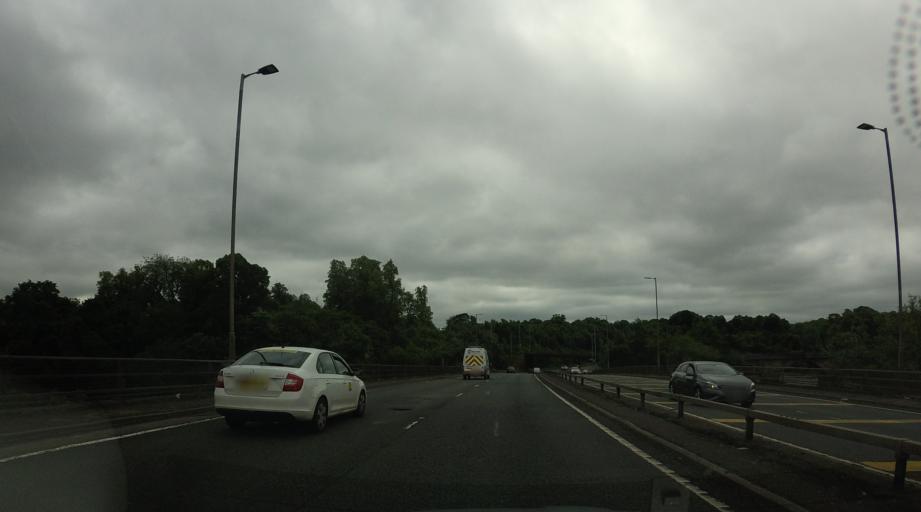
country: GB
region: Scotland
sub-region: South Lanarkshire
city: Bothwell
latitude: 55.7967
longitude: -4.0557
